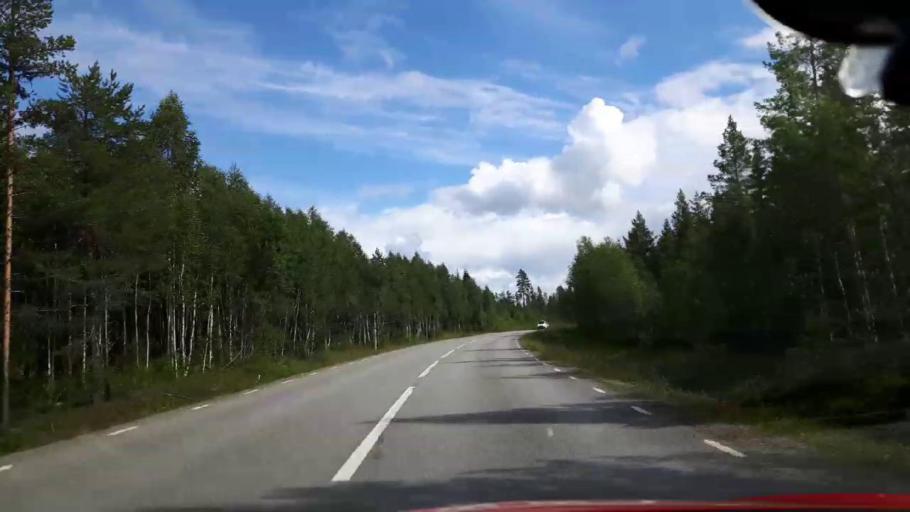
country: SE
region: Jaemtland
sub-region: Stroemsunds Kommun
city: Stroemsund
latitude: 64.3456
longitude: 15.1008
